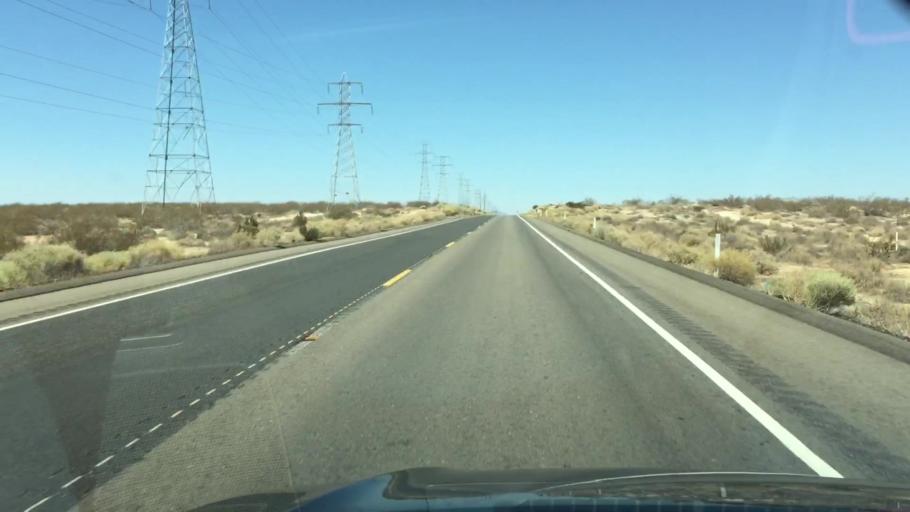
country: US
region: California
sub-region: Kern County
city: Boron
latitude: 35.0904
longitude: -117.5689
